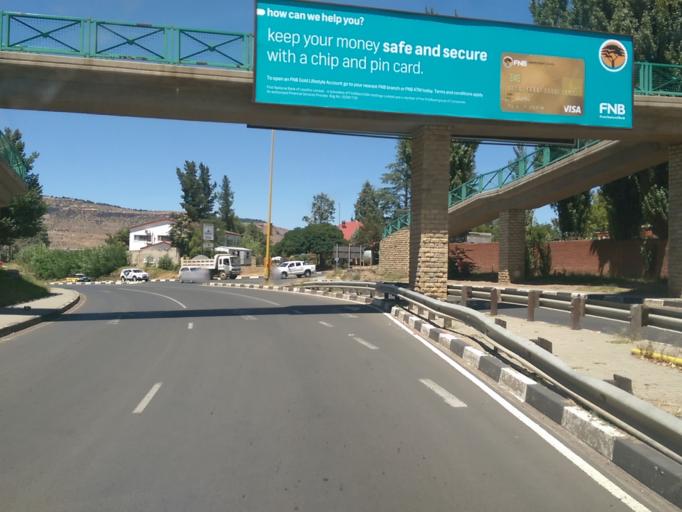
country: LS
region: Maseru
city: Maseru
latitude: -29.3133
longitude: 27.4773
